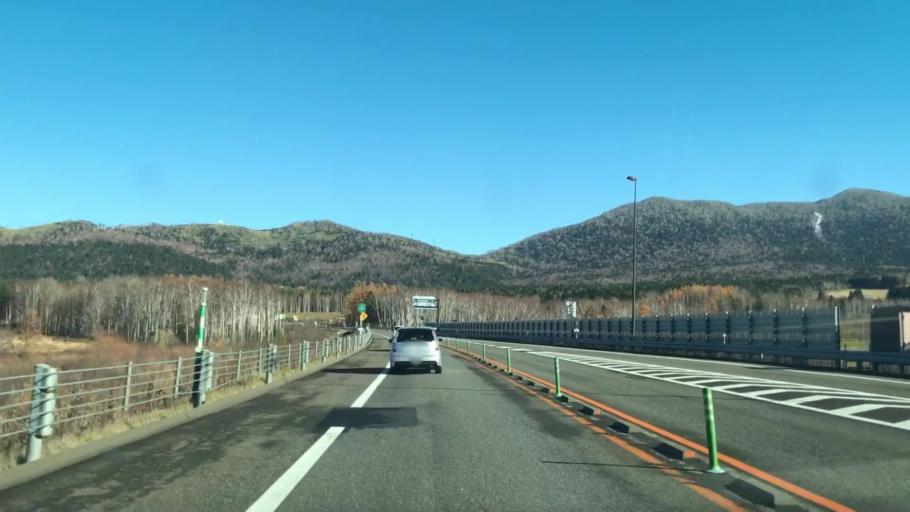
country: JP
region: Hokkaido
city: Shimo-furano
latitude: 43.0432
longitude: 142.6658
